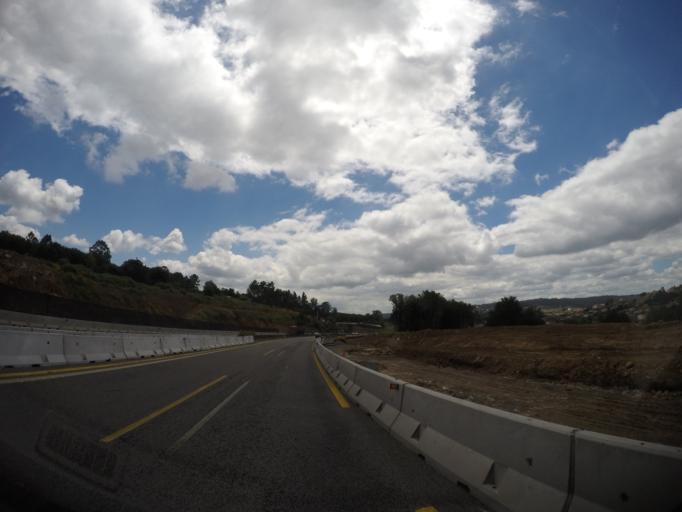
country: ES
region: Galicia
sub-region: Provincia da Coruna
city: Rois
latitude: 42.8251
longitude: -8.7516
